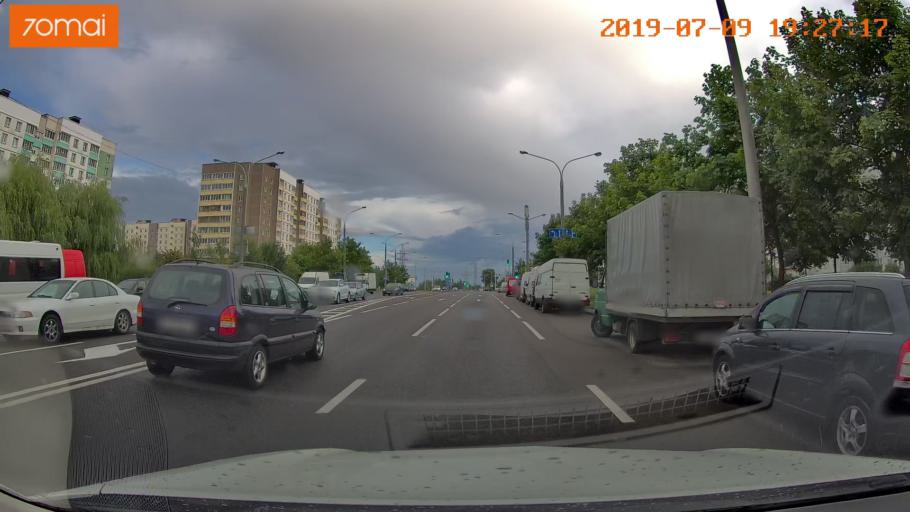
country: BY
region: Minsk
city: Syenitsa
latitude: 53.8380
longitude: 27.5744
